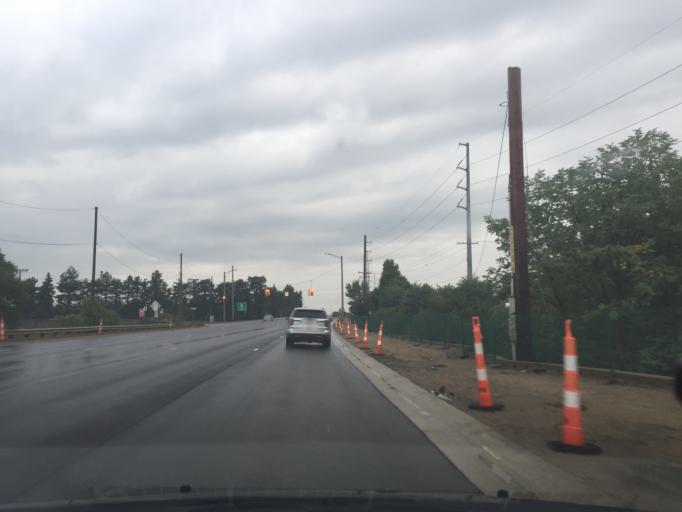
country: US
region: Michigan
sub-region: Oakland County
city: Pontiac
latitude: 42.6424
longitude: -83.2498
